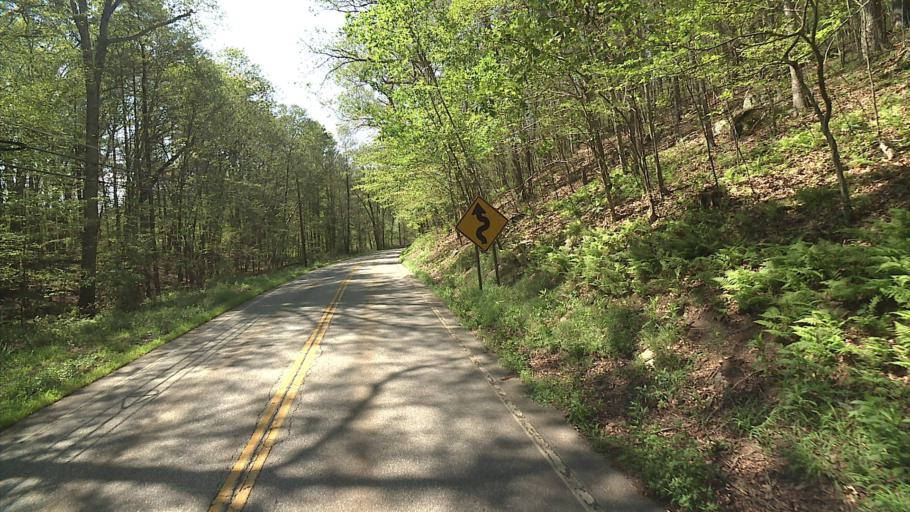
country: US
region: Connecticut
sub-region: Tolland County
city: Mansfield City
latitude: 41.8107
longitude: -72.1690
